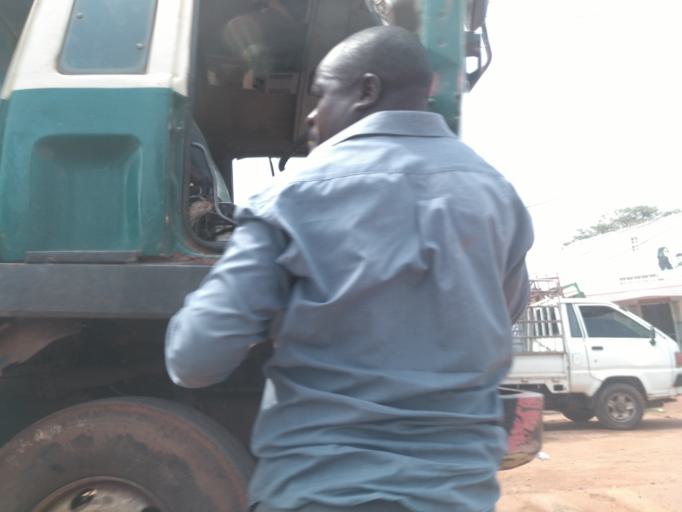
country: UG
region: Central Region
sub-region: Wakiso District
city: Kireka
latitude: 0.4512
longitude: 32.6102
